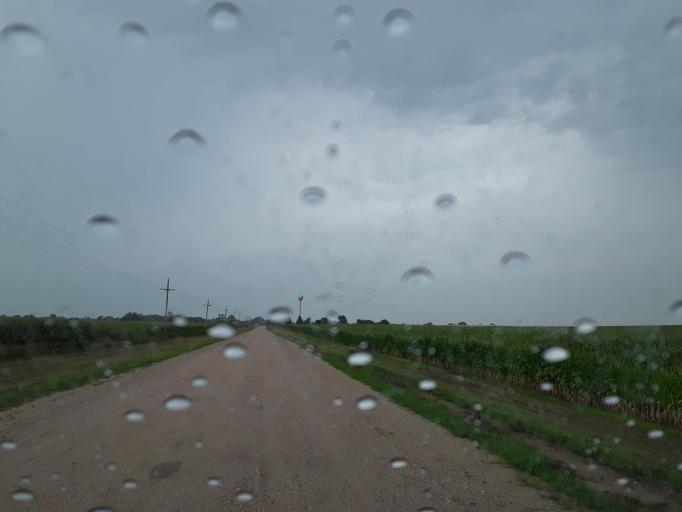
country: US
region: Nebraska
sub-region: Saunders County
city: Yutan
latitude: 41.1766
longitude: -96.4449
